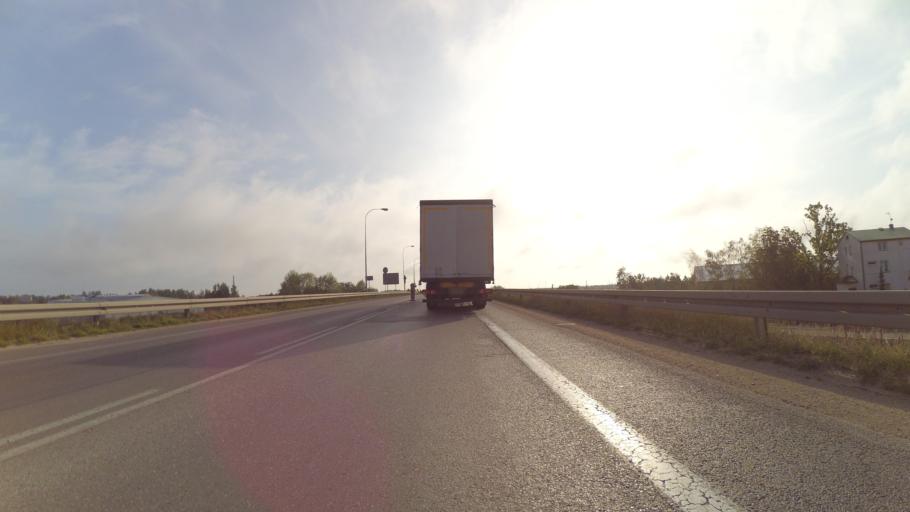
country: PL
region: Podlasie
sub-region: Powiat bialostocki
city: Dobrzyniewo Duze
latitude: 53.1509
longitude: 23.0695
